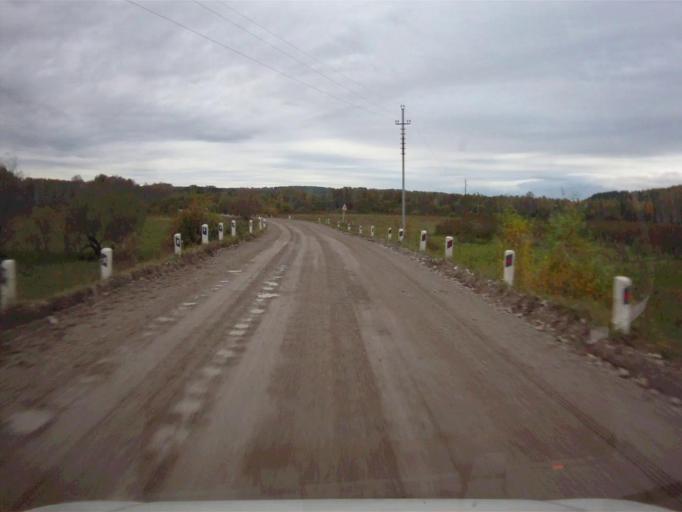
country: RU
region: Chelyabinsk
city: Nyazepetrovsk
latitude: 56.1249
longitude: 59.3539
